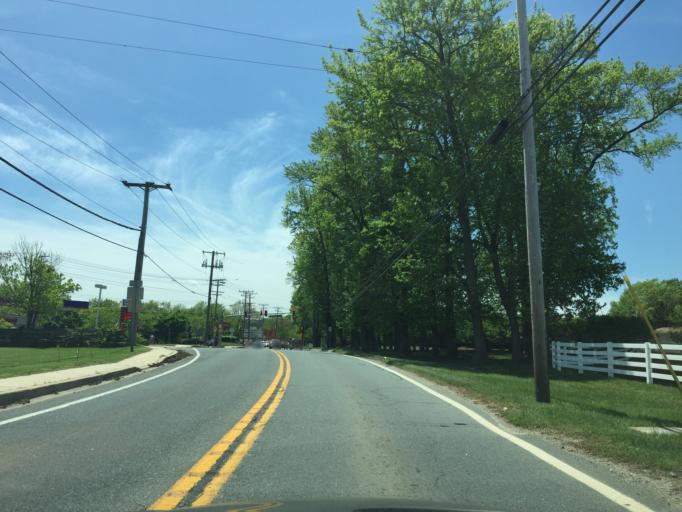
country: US
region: Maryland
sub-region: Baltimore County
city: Bowleys Quarters
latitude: 39.3394
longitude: -76.4017
